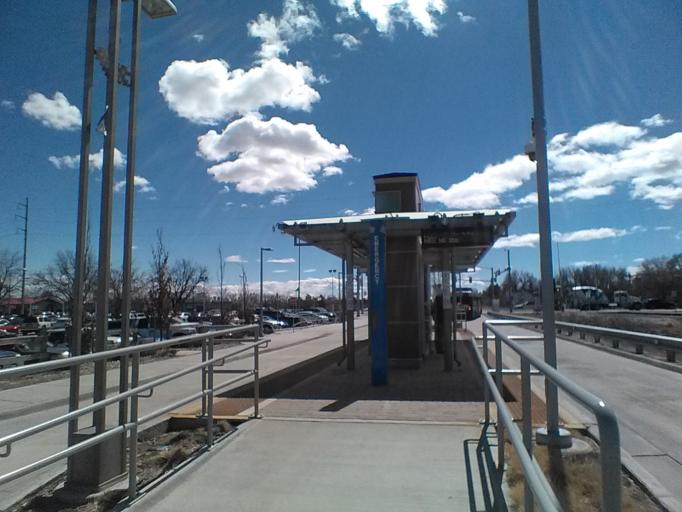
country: US
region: Colorado
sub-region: Larimer County
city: Fort Collins
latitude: 40.5533
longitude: -105.0798
